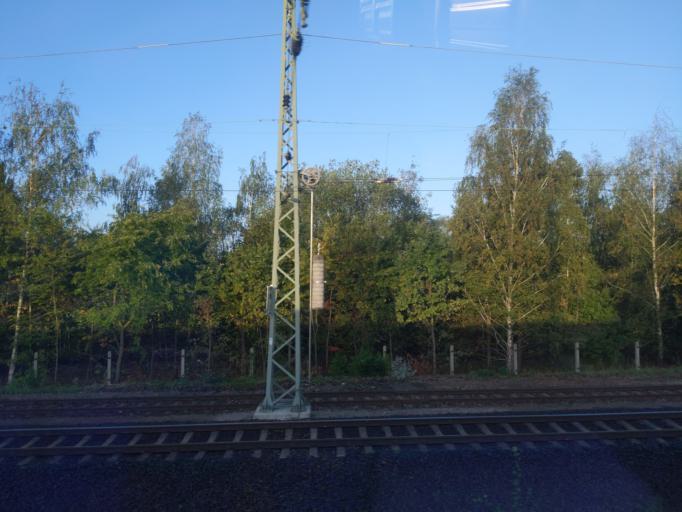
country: DE
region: Saxony
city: Coswig
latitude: 51.1286
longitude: 13.5728
